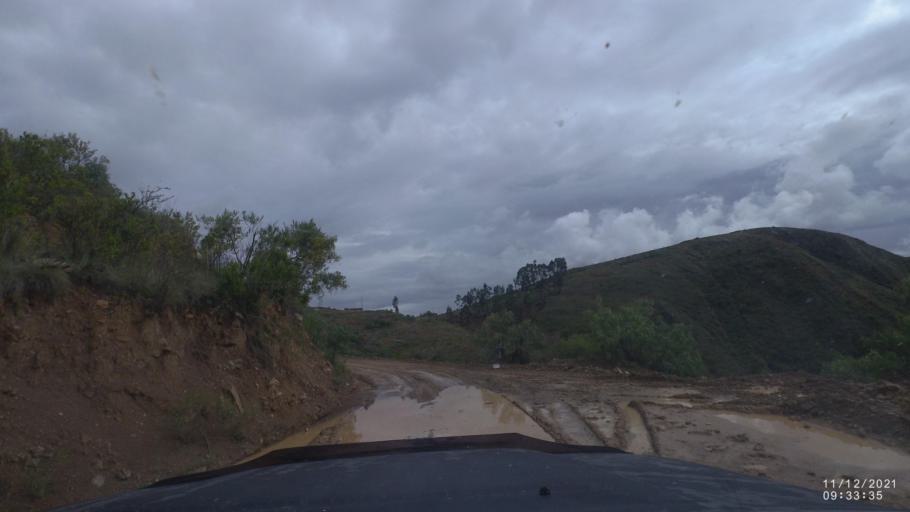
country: BO
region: Cochabamba
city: Tarata
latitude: -17.8378
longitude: -65.9928
